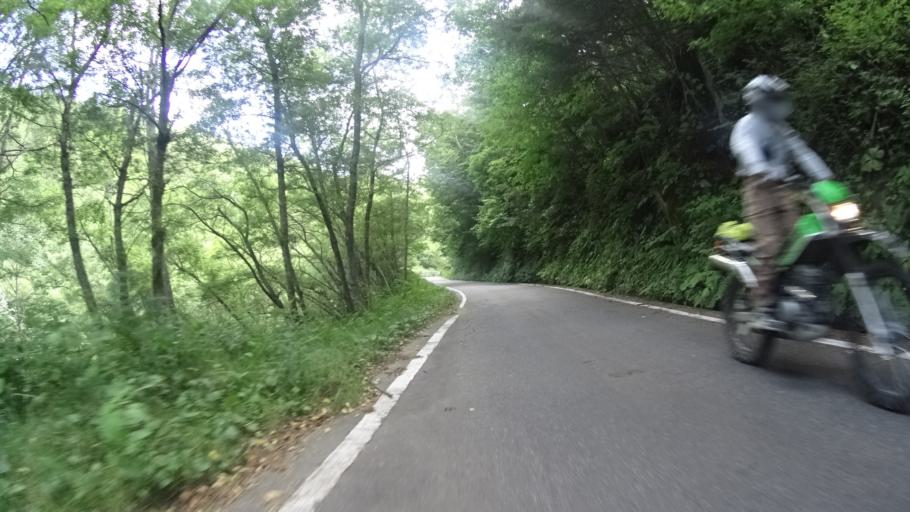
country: JP
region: Yamanashi
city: Enzan
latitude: 35.8390
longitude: 138.6439
